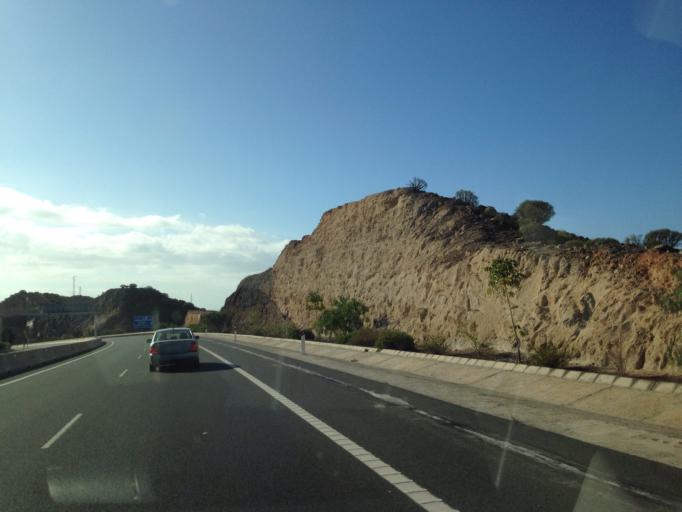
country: ES
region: Canary Islands
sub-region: Provincia de Las Palmas
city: Puerto Rico
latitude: 27.7772
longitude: -15.6768
